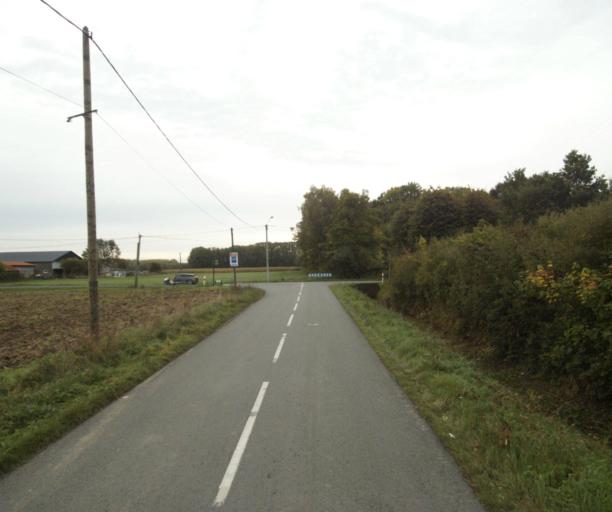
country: FR
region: Nord-Pas-de-Calais
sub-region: Departement du Pas-de-Calais
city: Lorgies
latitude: 50.5835
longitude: 2.7935
